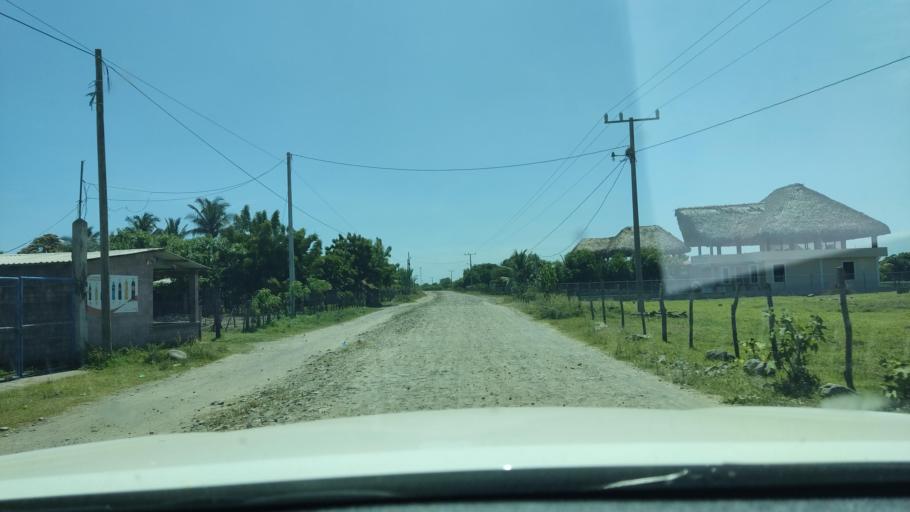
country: SV
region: Ahuachapan
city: San Francisco Menendez
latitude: 13.7646
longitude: -90.1670
